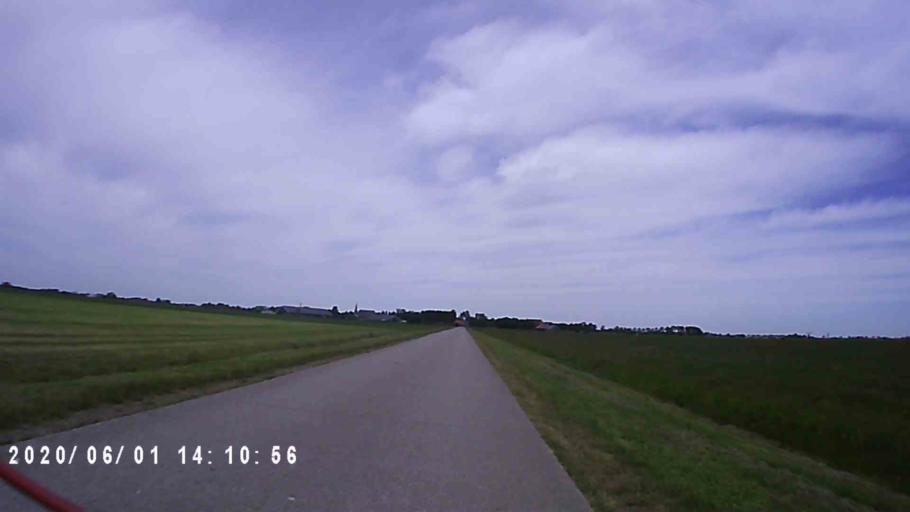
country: NL
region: Friesland
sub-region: Gemeente Littenseradiel
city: Winsum
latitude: 53.1253
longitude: 5.6488
